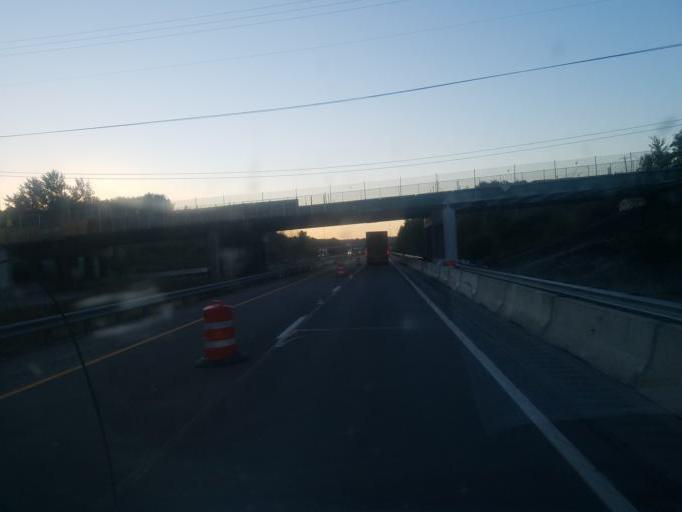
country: US
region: Ohio
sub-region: Mahoning County
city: Boardman
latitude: 40.9583
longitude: -80.6437
